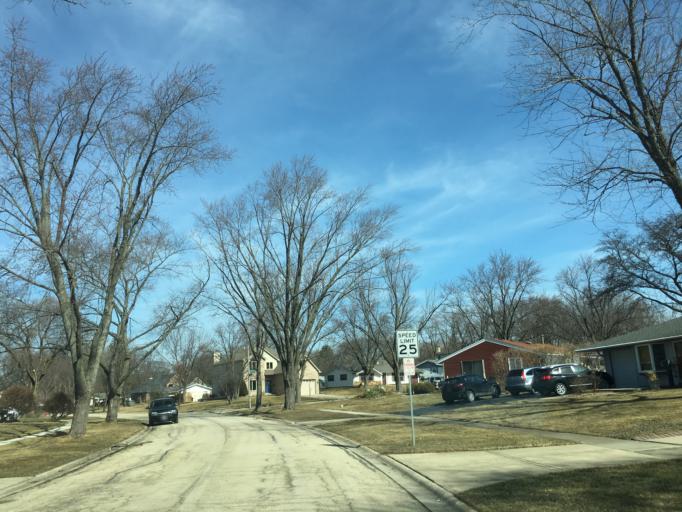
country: US
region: Illinois
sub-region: DuPage County
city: Hanover Park
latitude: 42.0203
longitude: -88.1265
